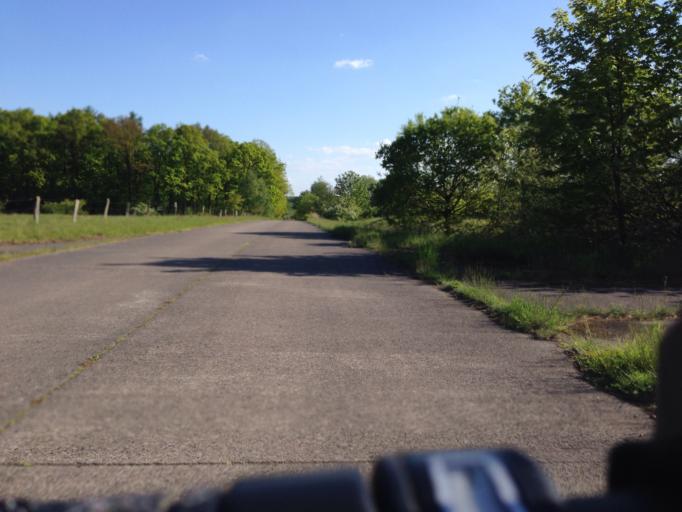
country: DE
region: Schleswig-Holstein
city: Stapelfeld
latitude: 53.6281
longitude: 10.2079
